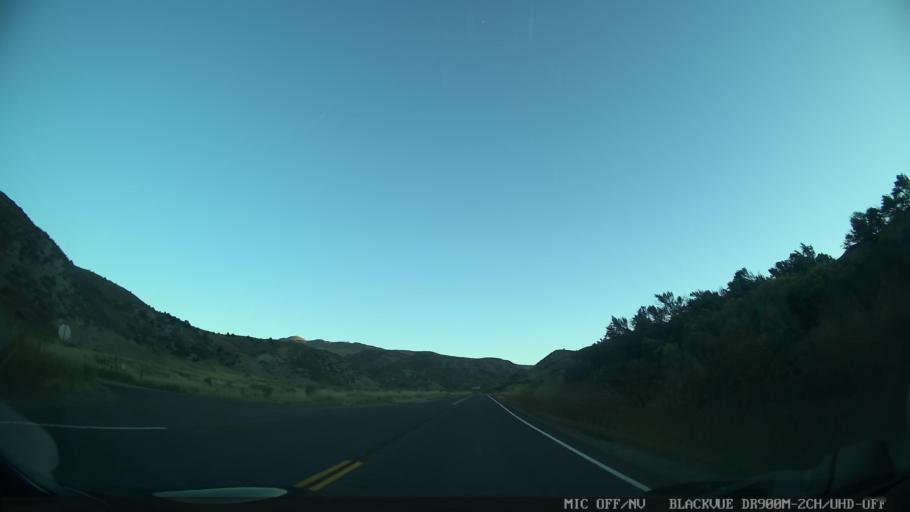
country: US
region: Colorado
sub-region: Eagle County
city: Edwards
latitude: 39.7919
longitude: -106.6797
